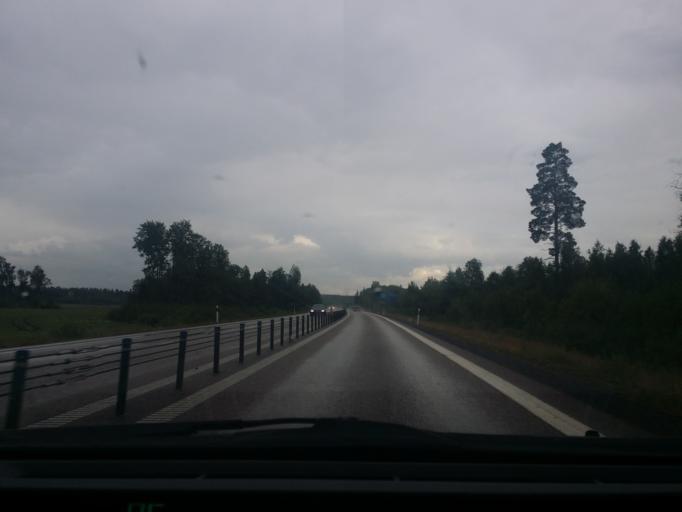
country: SE
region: Vaestmanland
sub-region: Arboga Kommun
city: Arboga
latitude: 59.4141
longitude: 15.8850
